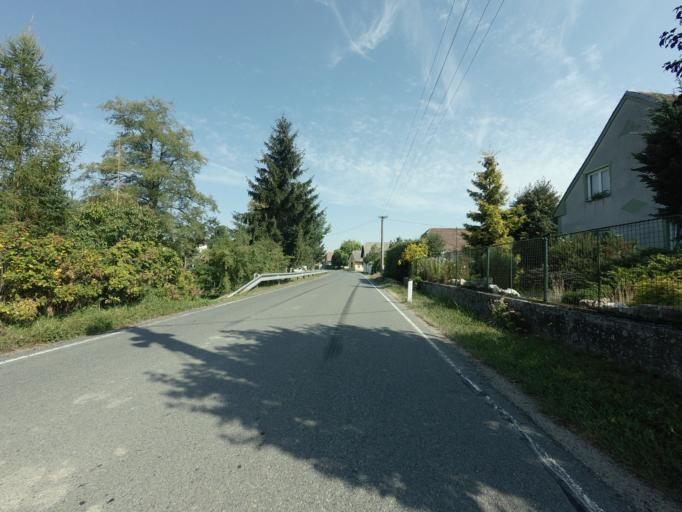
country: CZ
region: Jihocesky
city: Bernartice
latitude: 49.3578
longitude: 14.3776
